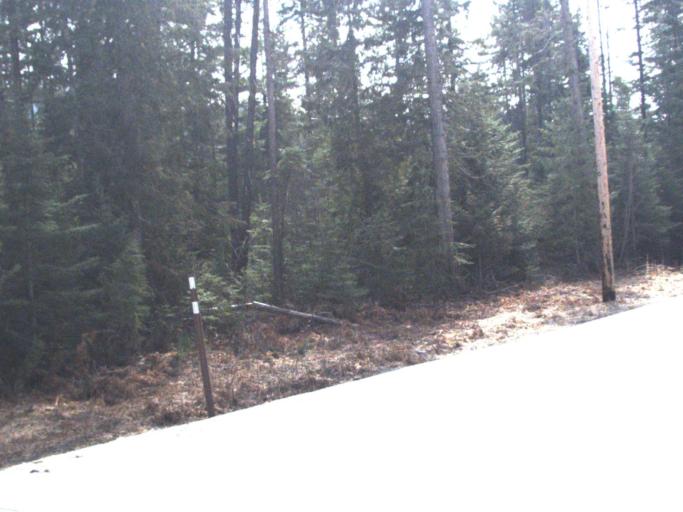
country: US
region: Washington
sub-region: Stevens County
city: Chewelah
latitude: 48.5810
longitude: -117.3513
